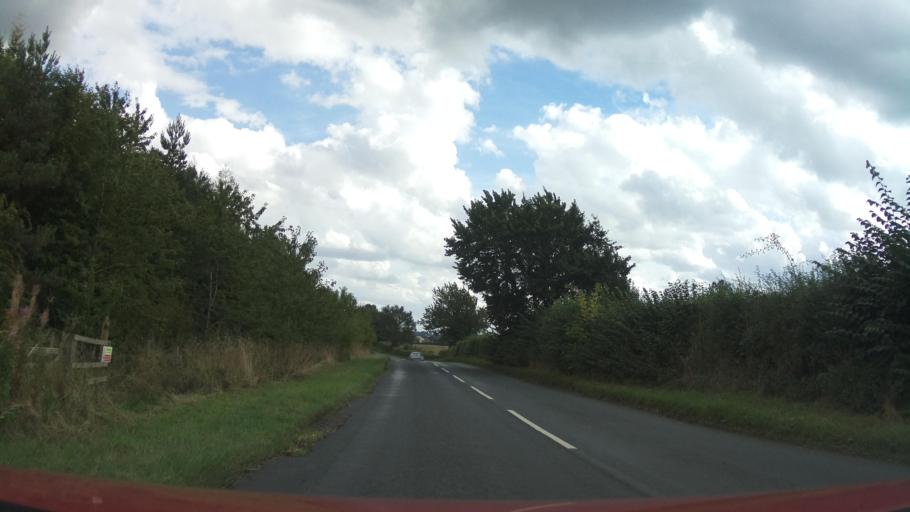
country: GB
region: England
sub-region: North Yorkshire
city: Bedale
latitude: 54.2400
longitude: -1.6831
